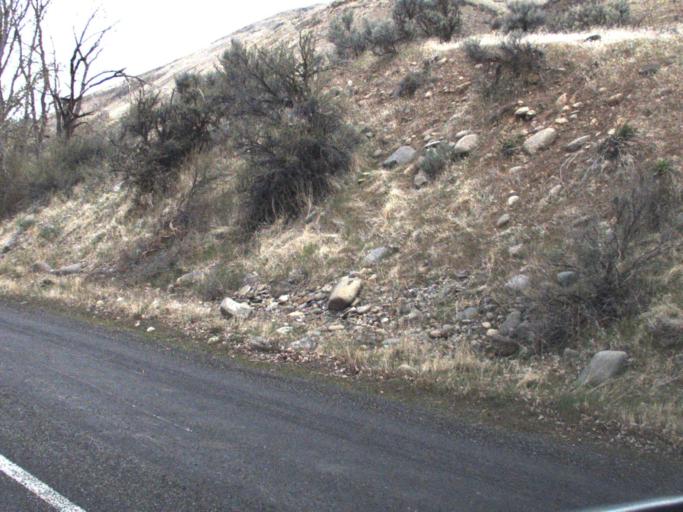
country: US
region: Washington
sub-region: Yakima County
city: Tieton
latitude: 46.7484
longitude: -120.7953
